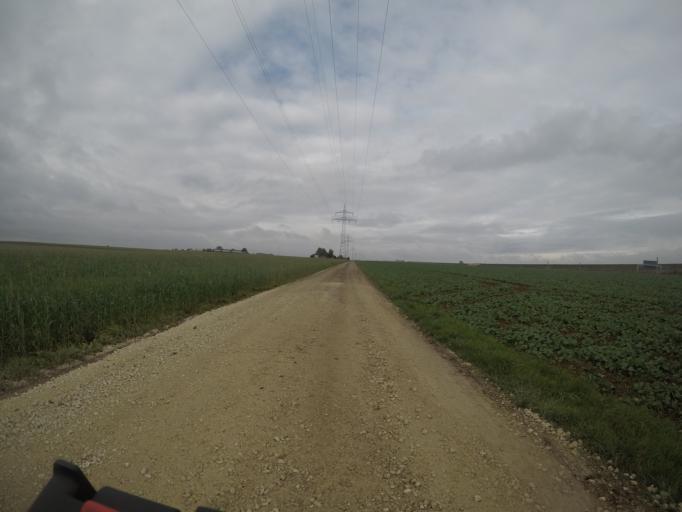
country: DE
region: Baden-Wuerttemberg
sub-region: Tuebingen Region
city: Dornstadt
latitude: 48.4581
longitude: 9.9366
